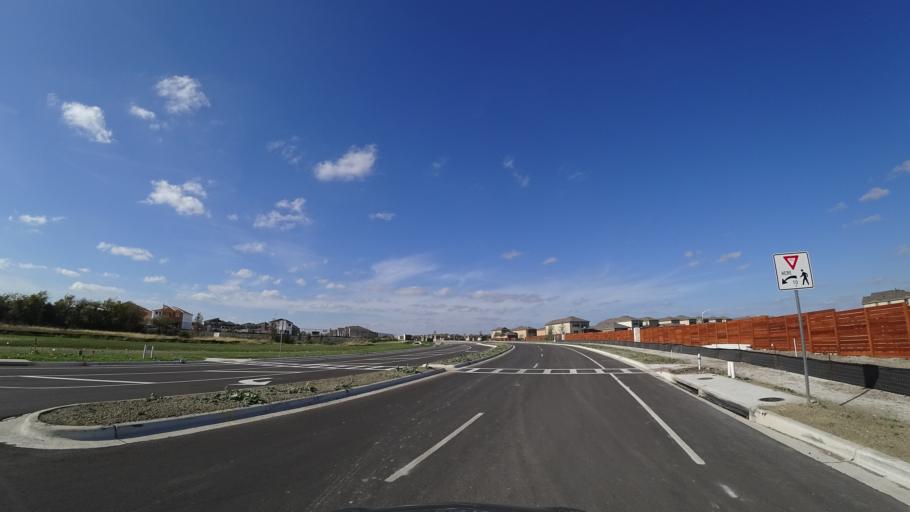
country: US
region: Texas
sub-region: Travis County
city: Wells Branch
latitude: 30.4645
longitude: -97.6802
